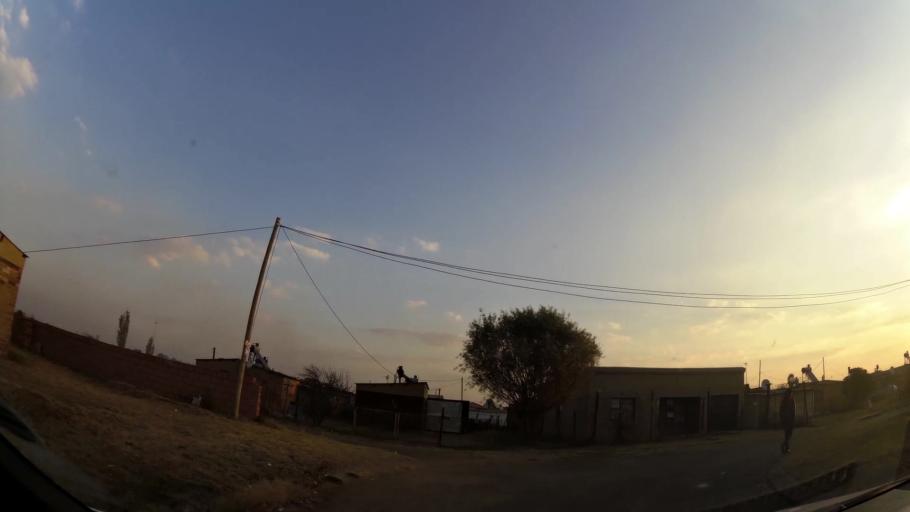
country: ZA
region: Gauteng
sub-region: Ekurhuleni Metropolitan Municipality
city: Springs
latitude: -26.2661
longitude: 28.3911
